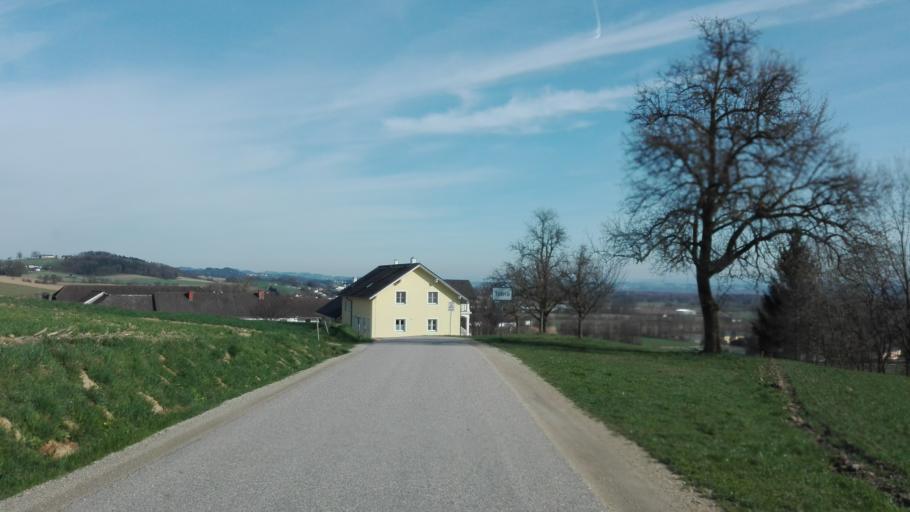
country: AT
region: Upper Austria
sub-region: Politischer Bezirk Perg
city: Perg
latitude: 48.2330
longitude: 14.6832
